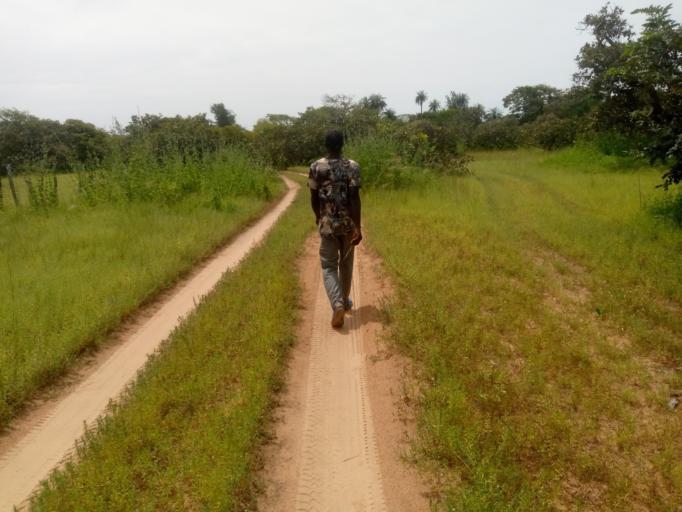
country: GM
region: Western
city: Gunjur
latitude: 13.0471
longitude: -16.7343
